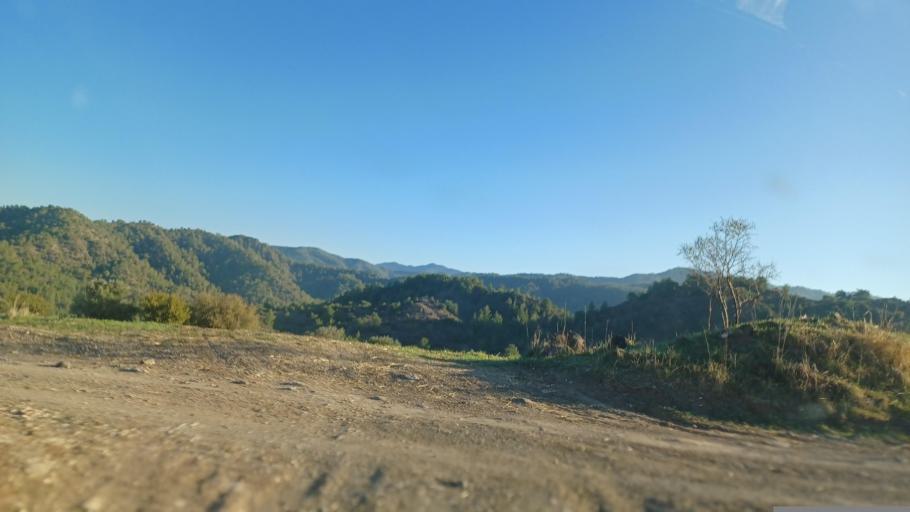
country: CY
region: Pafos
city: Polis
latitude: 34.9491
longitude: 32.5564
